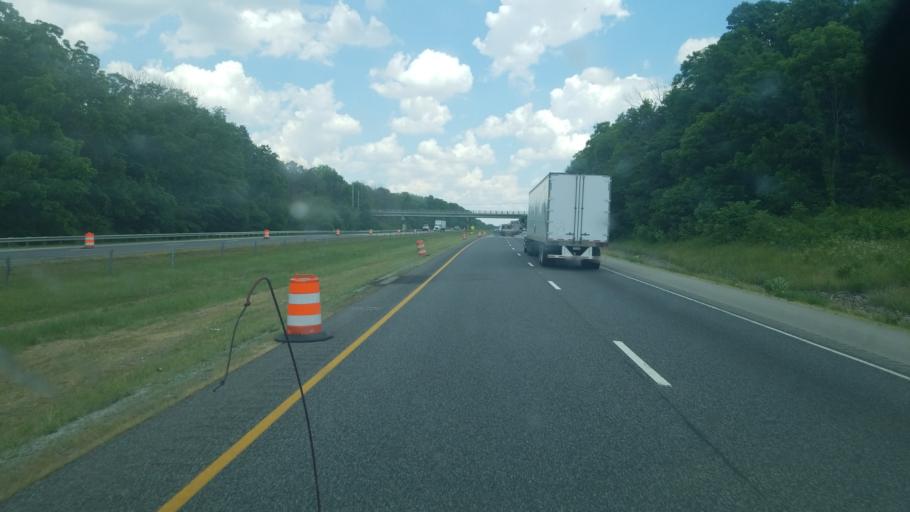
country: US
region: Indiana
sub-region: Henry County
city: Knightstown
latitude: 39.8536
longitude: -85.4586
